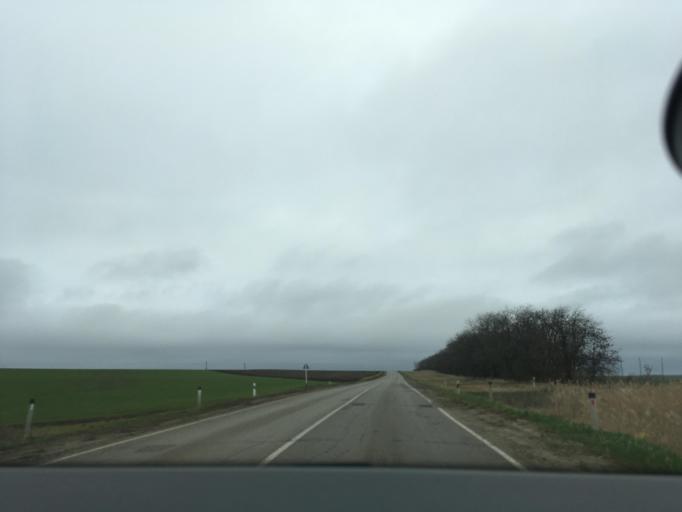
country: RU
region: Krasnodarskiy
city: Kushchevskaya
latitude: 46.5961
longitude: 39.6485
